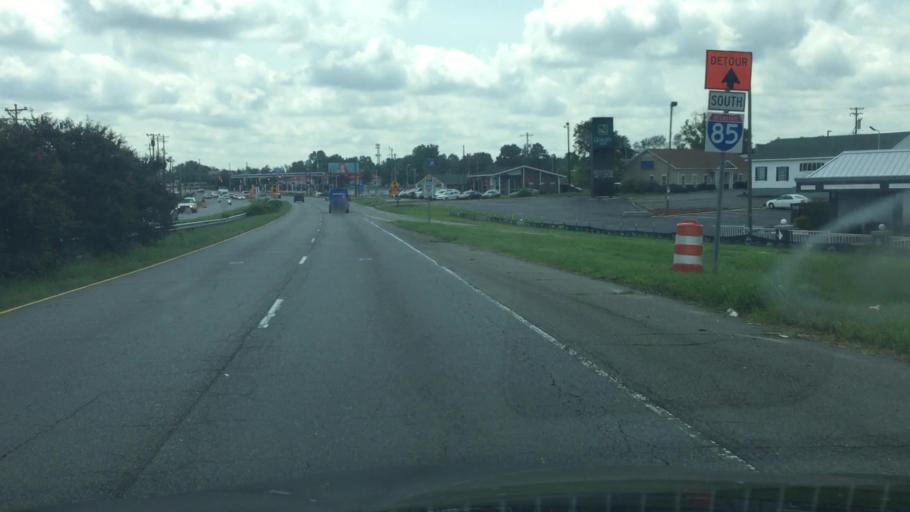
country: US
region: North Carolina
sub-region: Cabarrus County
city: Concord
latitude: 35.4440
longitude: -80.6090
